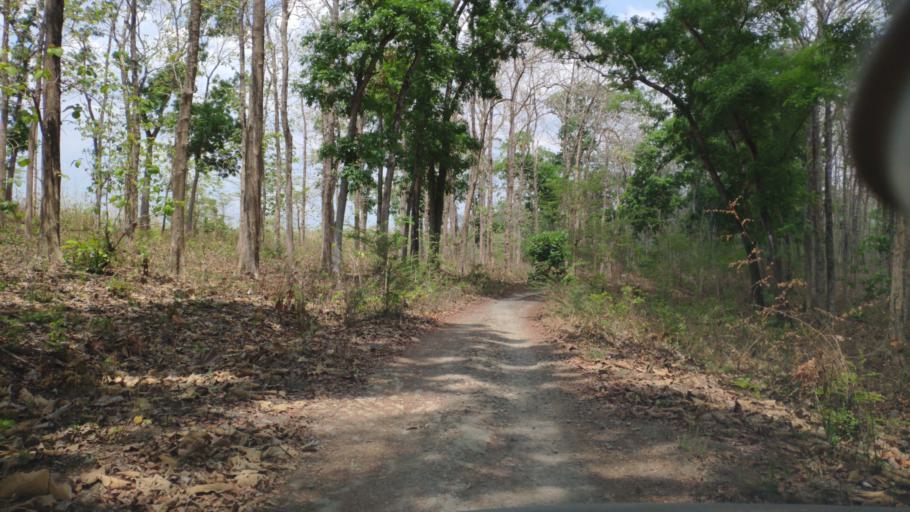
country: ID
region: Central Java
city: Singonegoro
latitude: -6.9924
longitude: 111.5320
